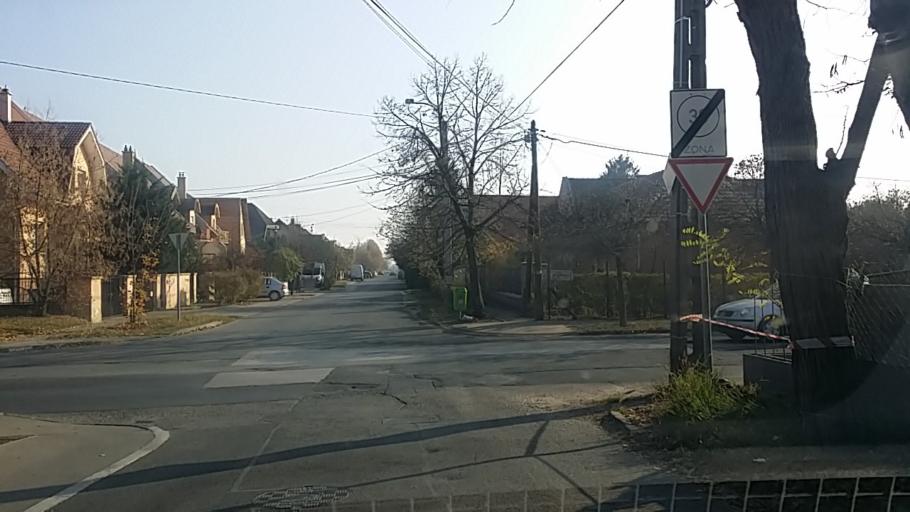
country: HU
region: Pest
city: Gyal
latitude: 47.4126
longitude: 19.1992
